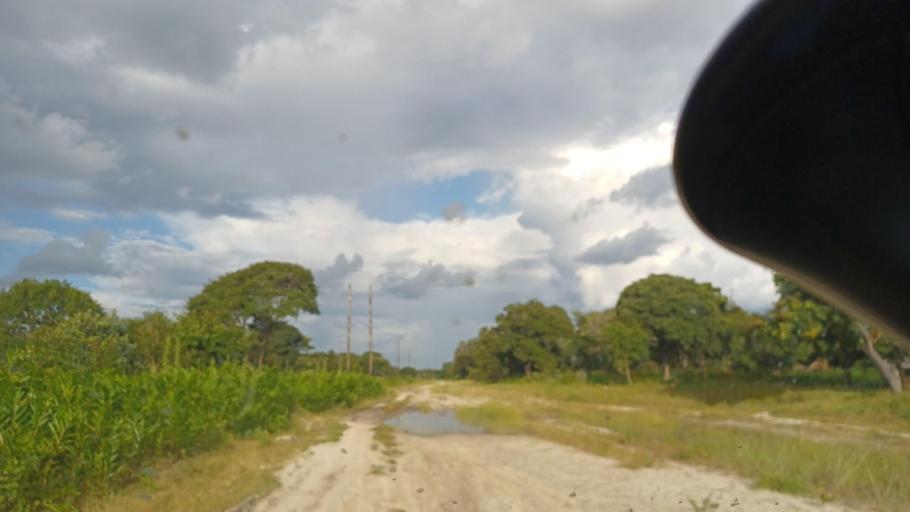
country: ZM
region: North-Western
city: Kabompo
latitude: -13.2471
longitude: 24.0292
